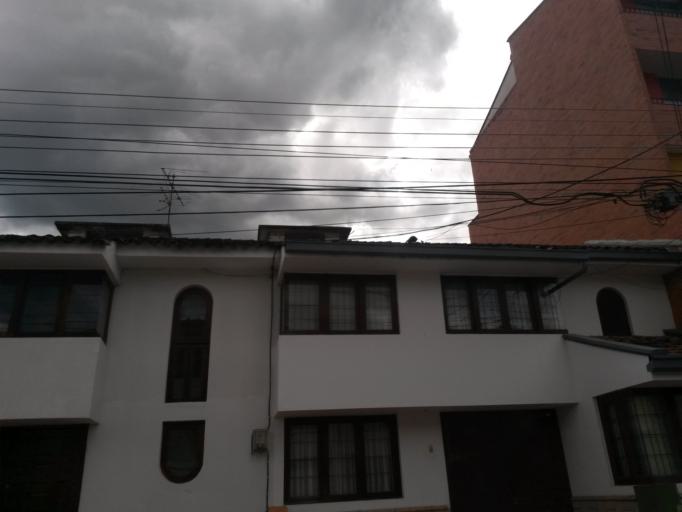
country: CO
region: Cauca
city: Popayan
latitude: 2.4455
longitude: -76.6016
